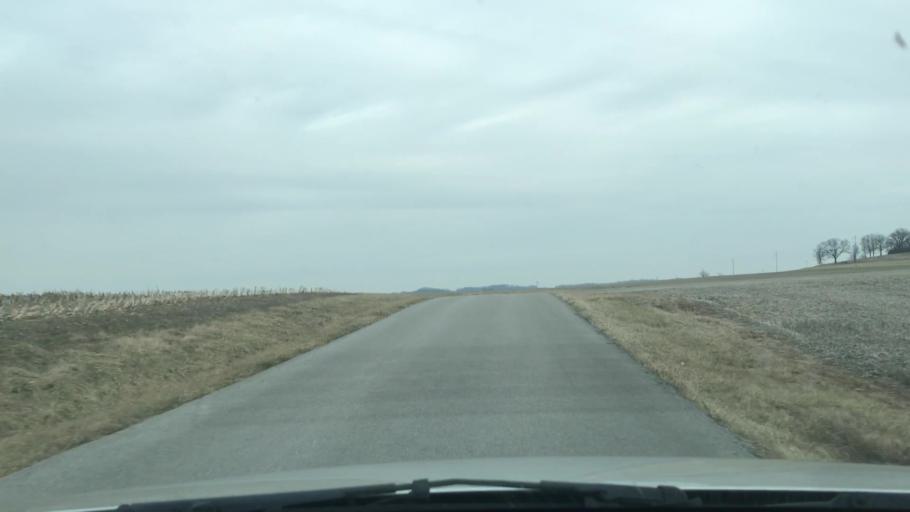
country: US
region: Kentucky
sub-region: Edmonson County
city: Brownsville
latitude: 37.0521
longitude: -86.2405
